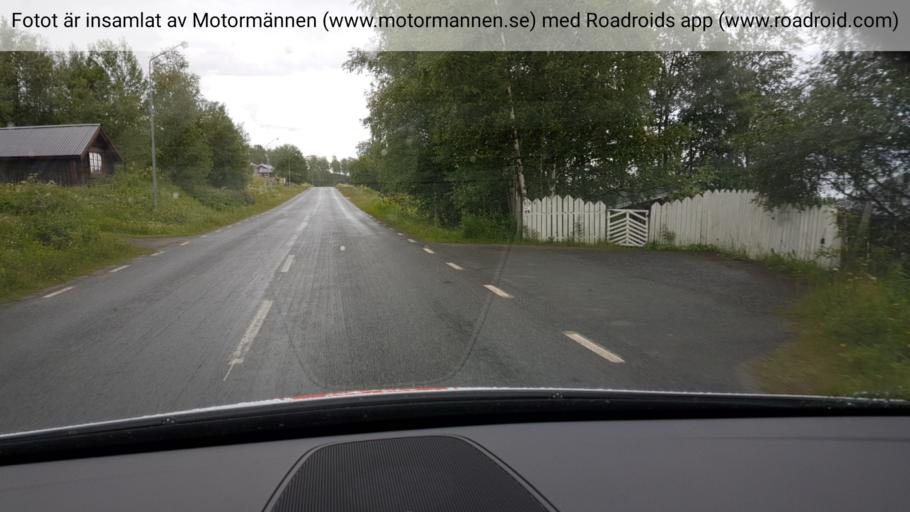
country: SE
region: Jaemtland
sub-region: Are Kommun
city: Are
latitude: 63.2169
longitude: 13.0465
